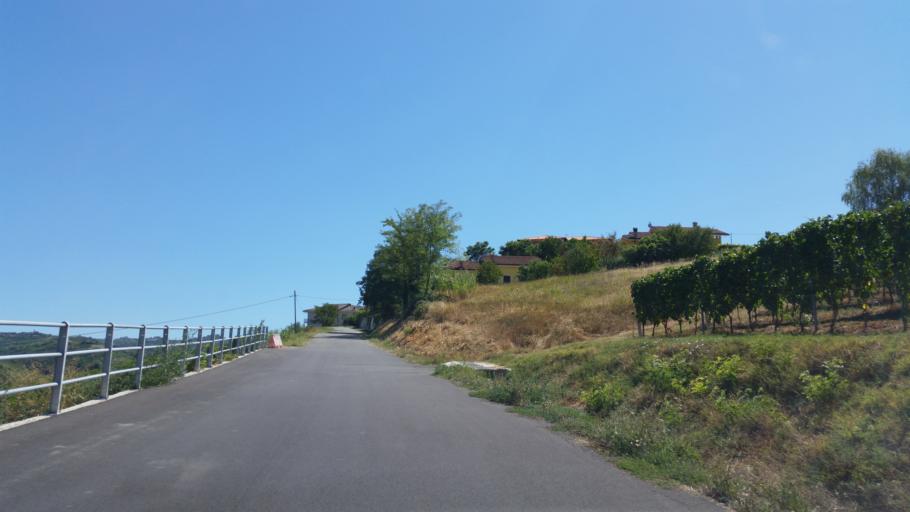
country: IT
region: Piedmont
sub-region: Provincia di Cuneo
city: Neive-Borgonovo
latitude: 44.7304
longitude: 8.1171
